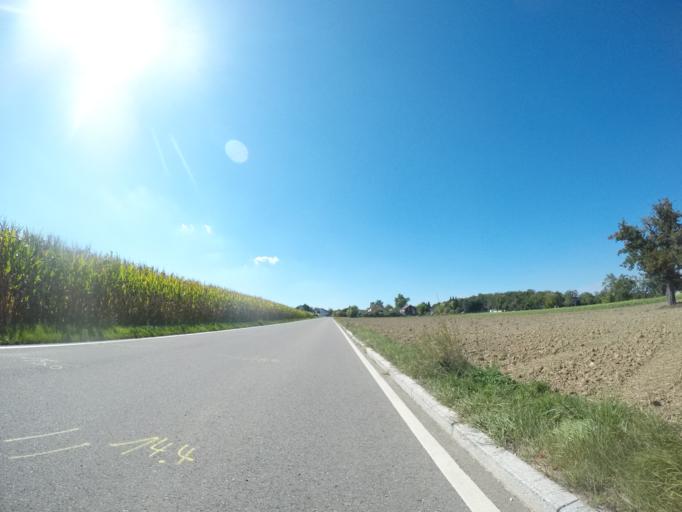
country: DE
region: Baden-Wuerttemberg
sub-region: Tuebingen Region
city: Kusterdingen
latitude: 48.5000
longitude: 9.0937
